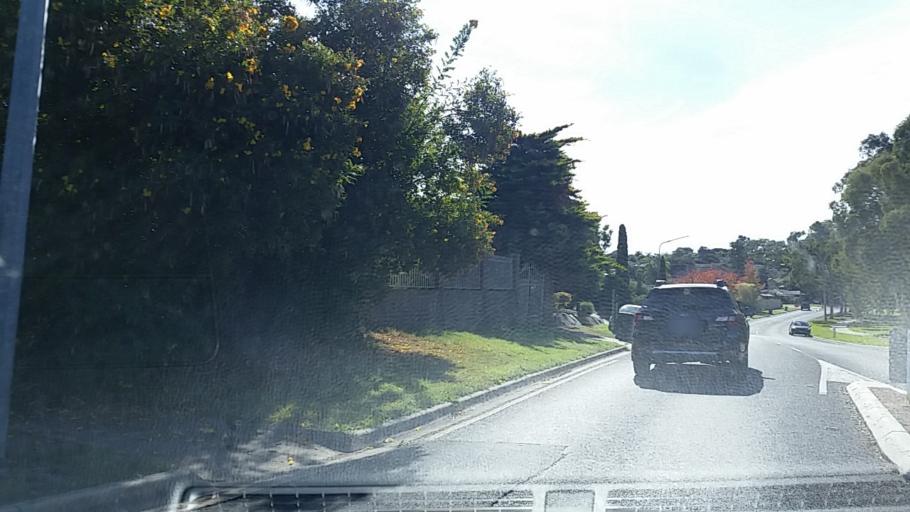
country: AU
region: South Australia
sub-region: Tea Tree Gully
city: Hope Valley
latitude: -34.8169
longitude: 138.6928
